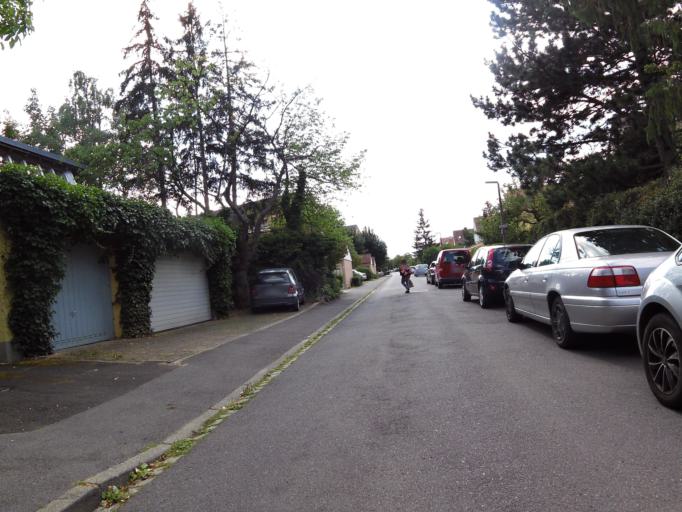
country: DE
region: Bavaria
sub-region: Regierungsbezirk Unterfranken
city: Gerbrunn
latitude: 49.7836
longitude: 9.9853
